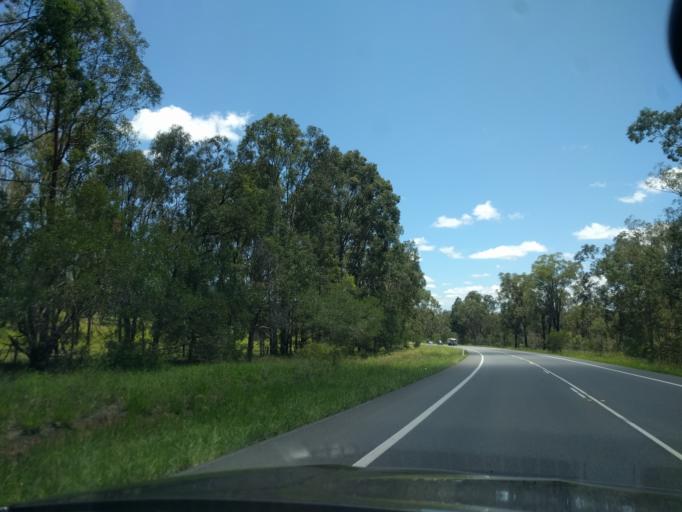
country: AU
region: Queensland
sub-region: Logan
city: Cedar Vale
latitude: -27.8705
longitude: 152.9980
